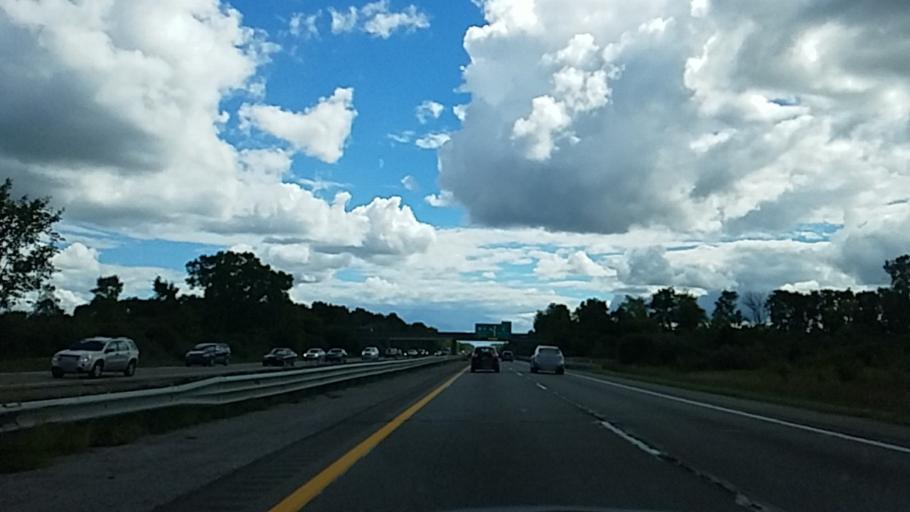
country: US
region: Michigan
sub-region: Washtenaw County
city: Ann Arbor
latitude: 42.3451
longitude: -83.7459
